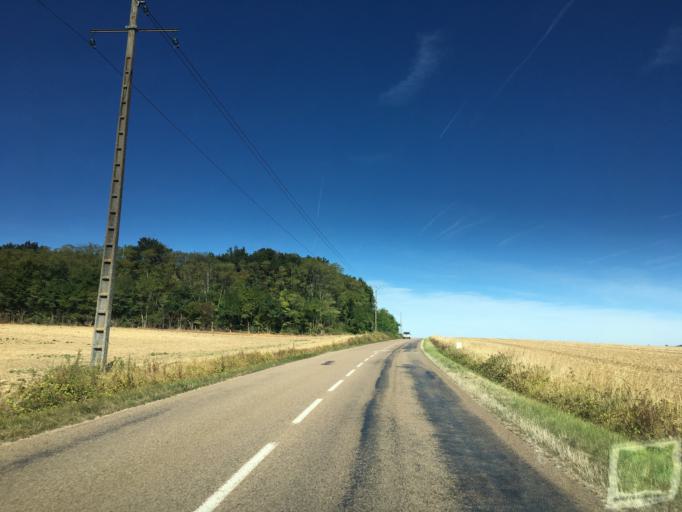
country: FR
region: Bourgogne
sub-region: Departement de l'Yonne
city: Saint-Bris-le-Vineux
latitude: 47.6739
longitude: 3.6580
